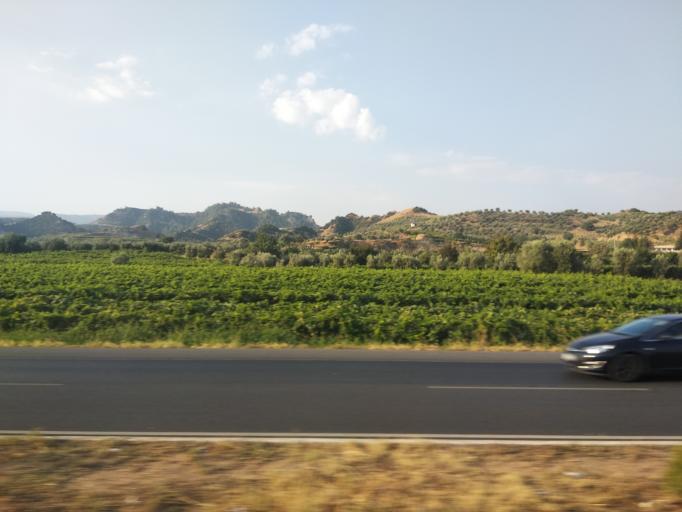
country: TR
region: Manisa
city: Ahmetli
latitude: 38.5078
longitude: 27.9888
